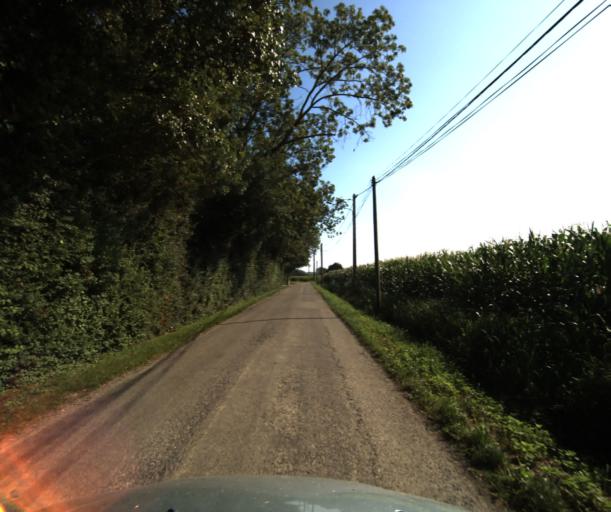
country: FR
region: Midi-Pyrenees
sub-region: Departement de la Haute-Garonne
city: Le Fauga
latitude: 43.4131
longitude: 1.3051
